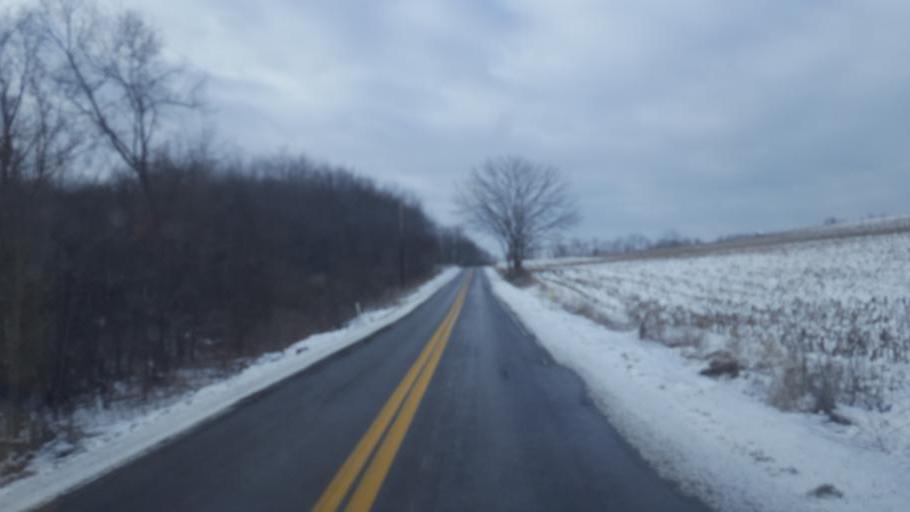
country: US
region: Pennsylvania
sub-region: Mercer County
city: Mercer
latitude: 41.1648
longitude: -80.2514
